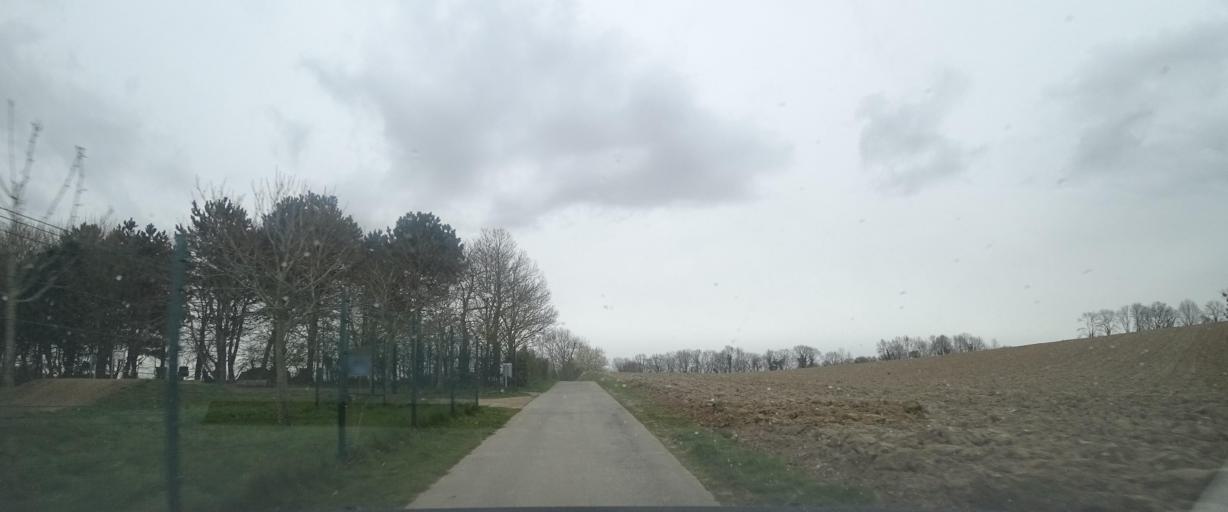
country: BE
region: Wallonia
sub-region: Province du Brabant Wallon
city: Mont-Saint-Guibert
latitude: 50.6356
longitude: 4.6041
